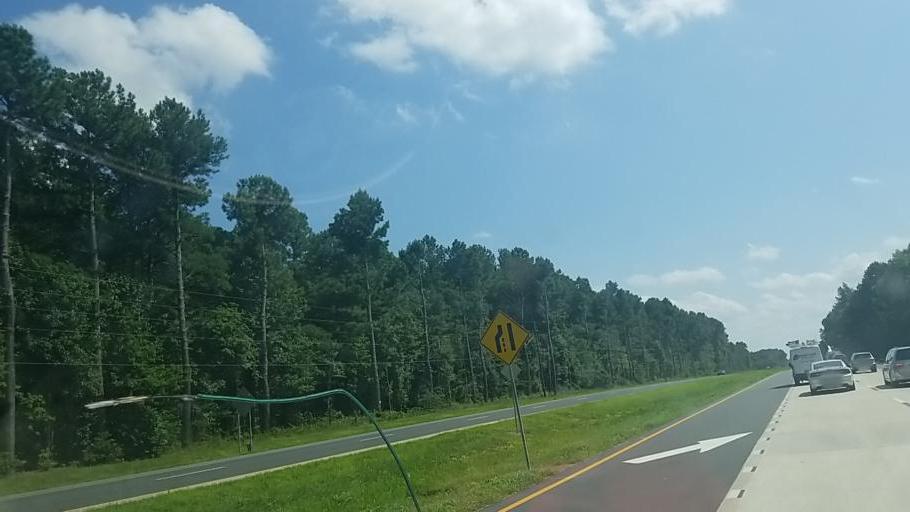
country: US
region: Delaware
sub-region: Sussex County
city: Milford
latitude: 38.8256
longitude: -75.4391
